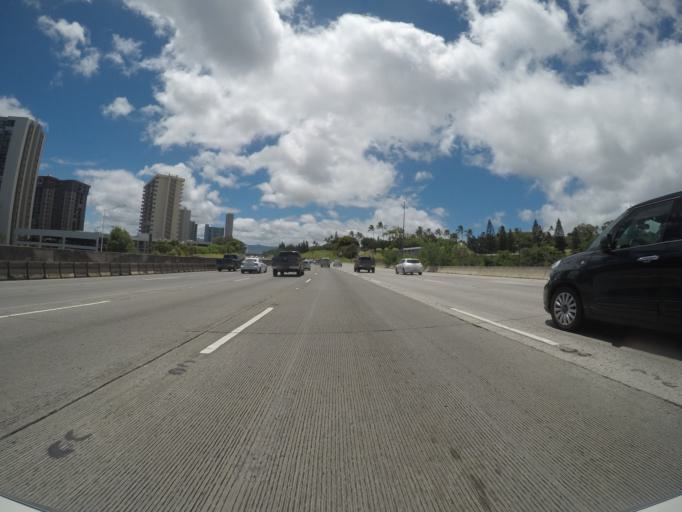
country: US
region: Hawaii
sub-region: Honolulu County
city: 'Aiea
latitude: 21.3857
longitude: -157.9338
